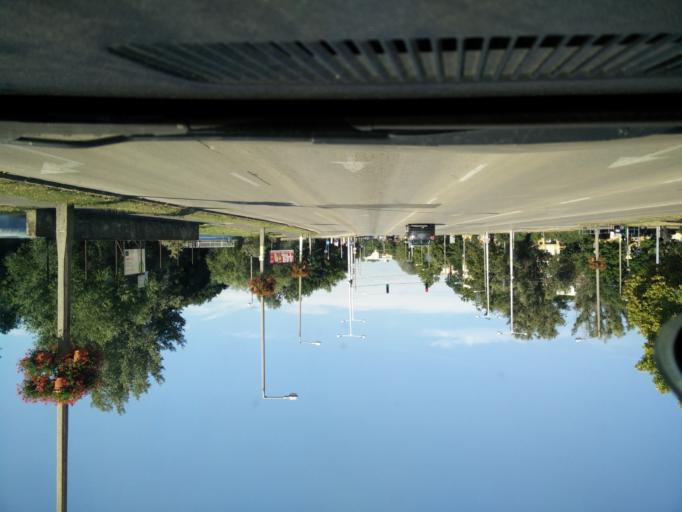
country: HU
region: Komarom-Esztergom
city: Tatabanya
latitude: 47.5763
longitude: 18.4032
